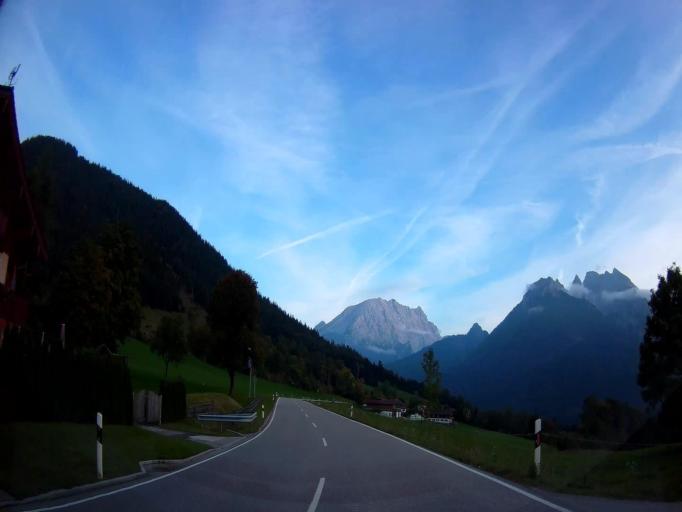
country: DE
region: Bavaria
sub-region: Upper Bavaria
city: Ramsau
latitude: 47.6271
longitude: 12.8776
